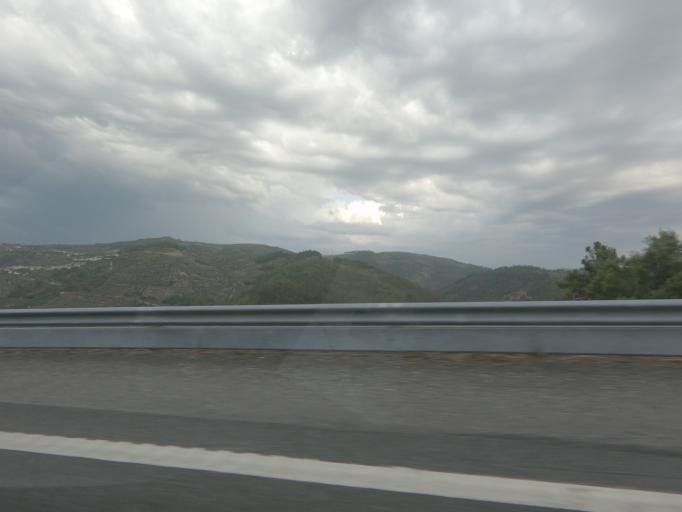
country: PT
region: Viseu
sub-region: Lamego
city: Lamego
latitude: 41.0976
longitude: -7.7811
